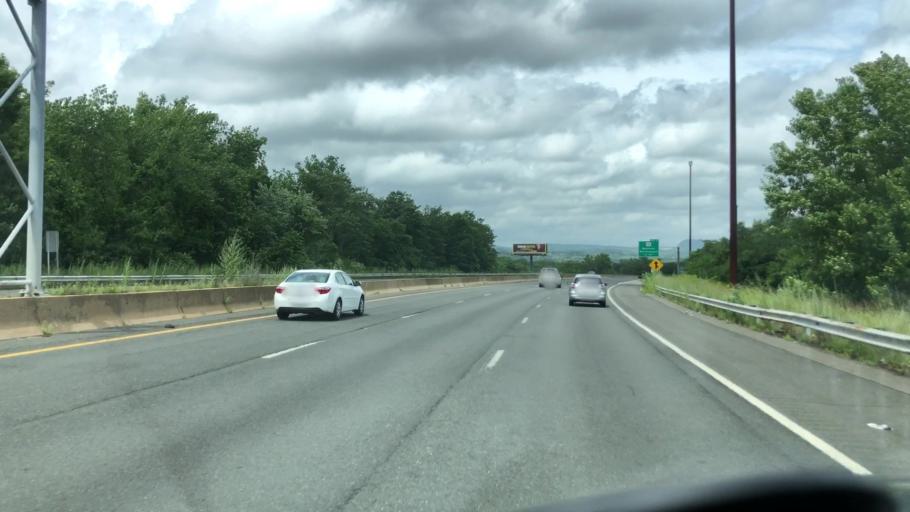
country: US
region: Massachusetts
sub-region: Hampden County
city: Chicopee
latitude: 42.1421
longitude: -72.6133
